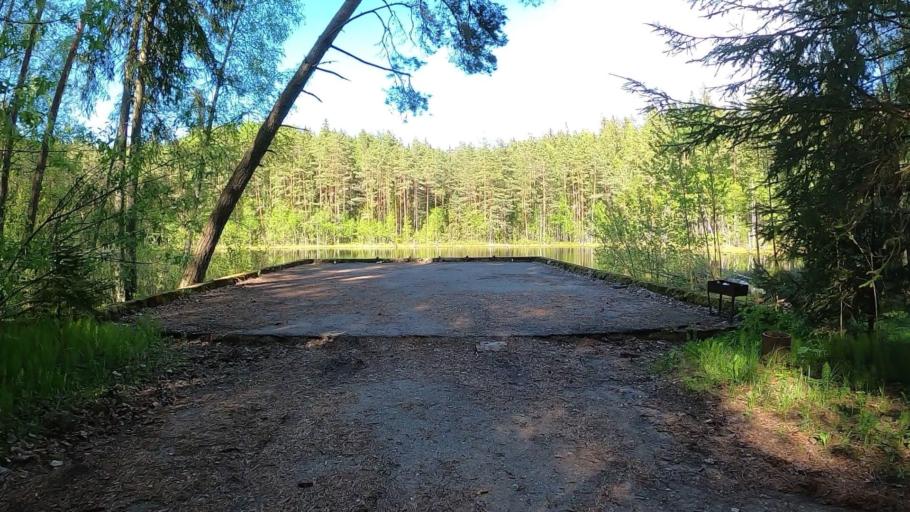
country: LV
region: Baldone
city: Baldone
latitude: 56.7725
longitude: 24.4118
